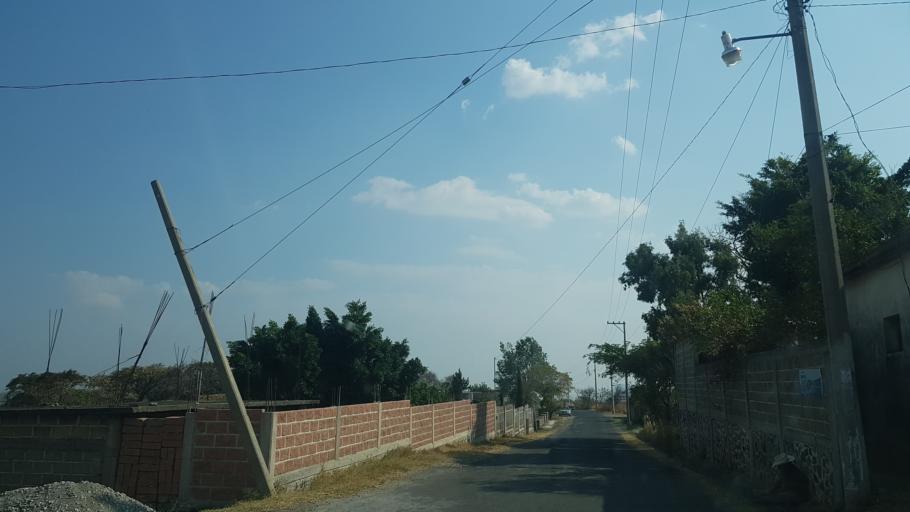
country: MX
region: Morelos
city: Tlacotepec
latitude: 18.8083
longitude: -98.7132
